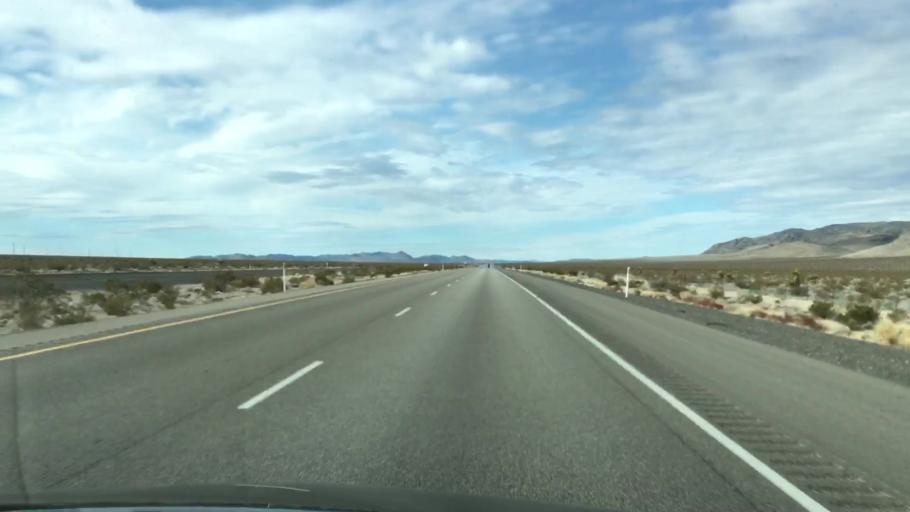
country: US
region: Nevada
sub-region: Nye County
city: Pahrump
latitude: 36.5872
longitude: -115.9170
